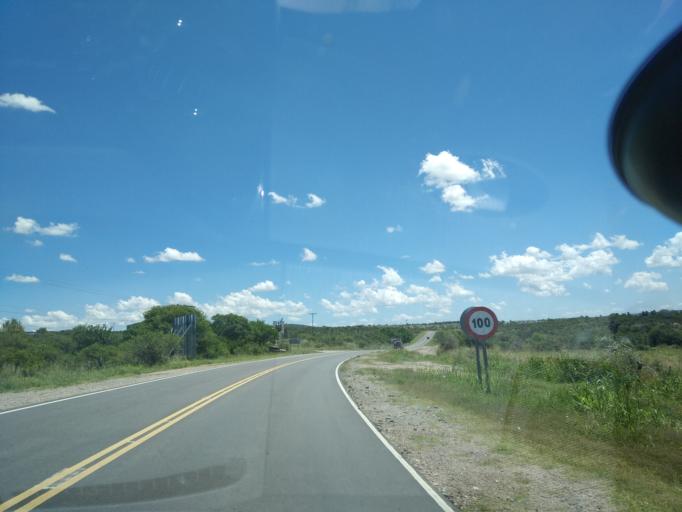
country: AR
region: Cordoba
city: Salsacate
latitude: -31.3475
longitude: -65.0806
